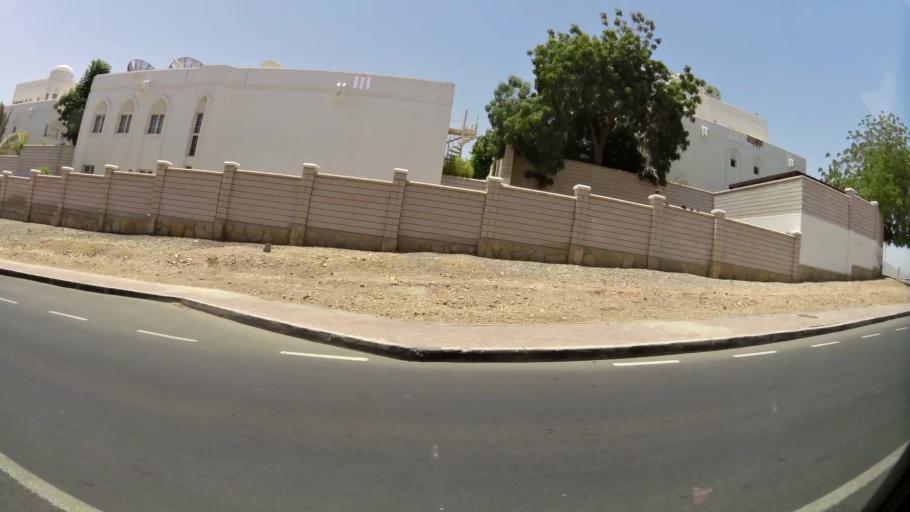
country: OM
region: Muhafazat Masqat
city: Bawshar
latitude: 23.6080
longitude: 58.4724
